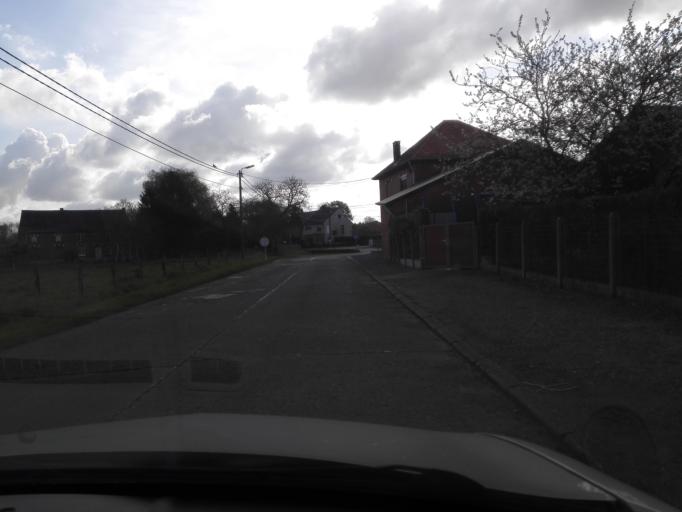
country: BE
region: Flanders
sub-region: Provincie Vlaams-Brabant
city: Bekkevoort
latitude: 50.9458
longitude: 4.9192
